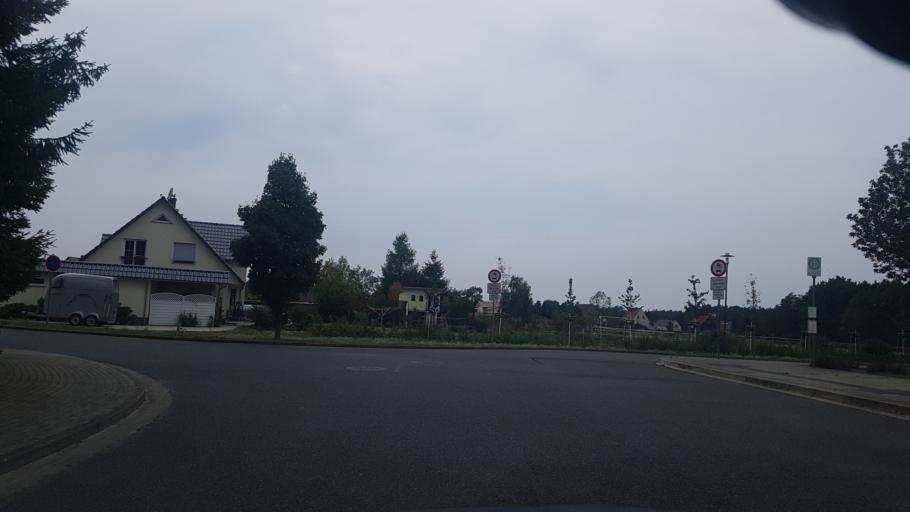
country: DE
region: Brandenburg
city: Guteborn
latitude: 51.4252
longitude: 13.9199
